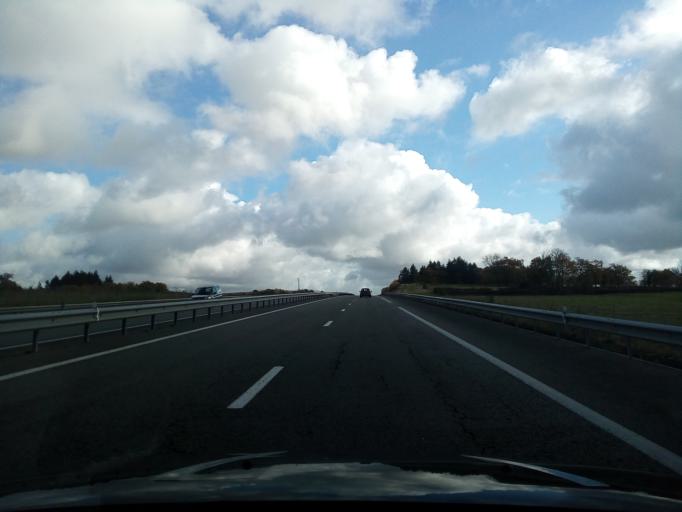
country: FR
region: Limousin
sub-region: Departement de la Creuse
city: Gouzon
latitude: 46.2000
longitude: 2.1242
